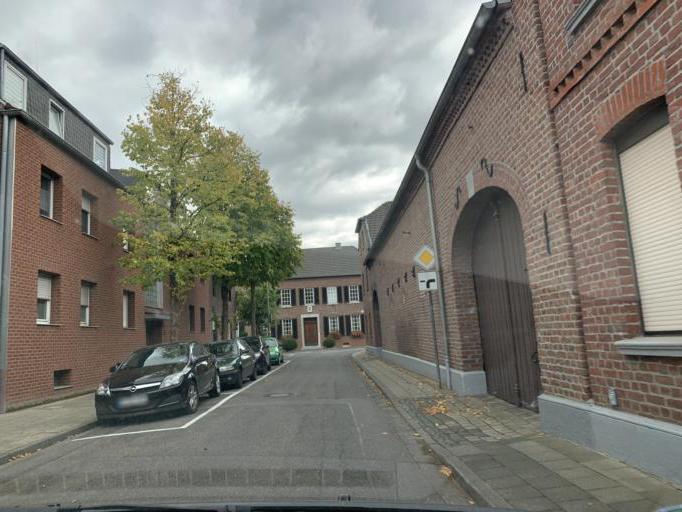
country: DE
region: North Rhine-Westphalia
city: Erkelenz
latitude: 51.1094
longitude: 6.3361
